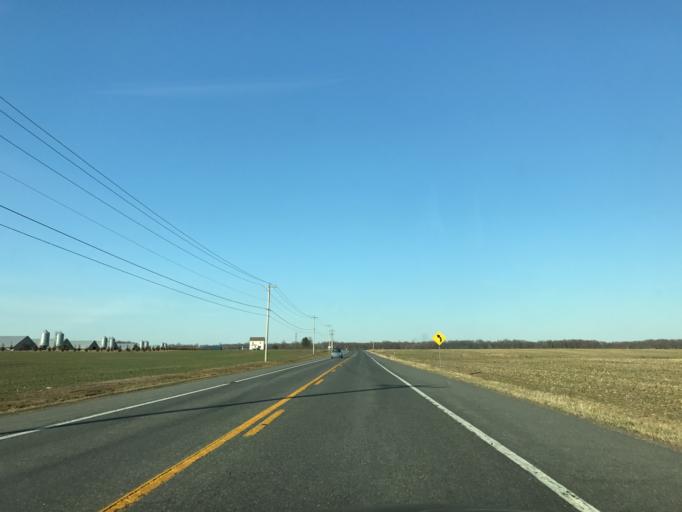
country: US
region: Maryland
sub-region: Caroline County
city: Greensboro
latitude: 39.1548
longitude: -75.8660
